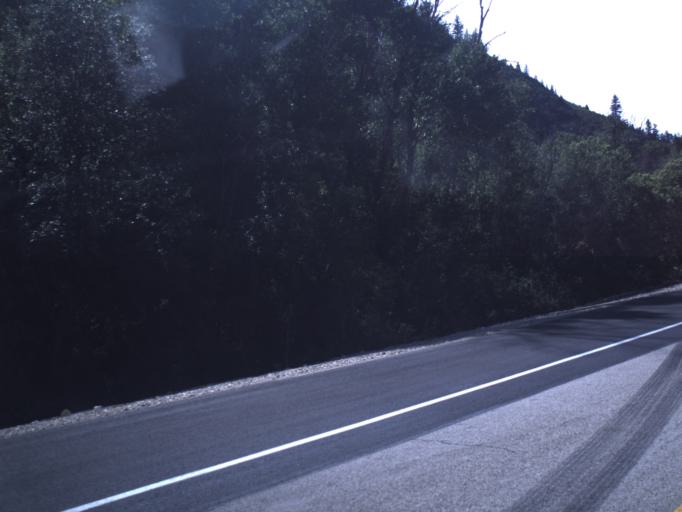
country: US
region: Utah
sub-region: Wasatch County
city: Heber
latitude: 40.4066
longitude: -111.3119
